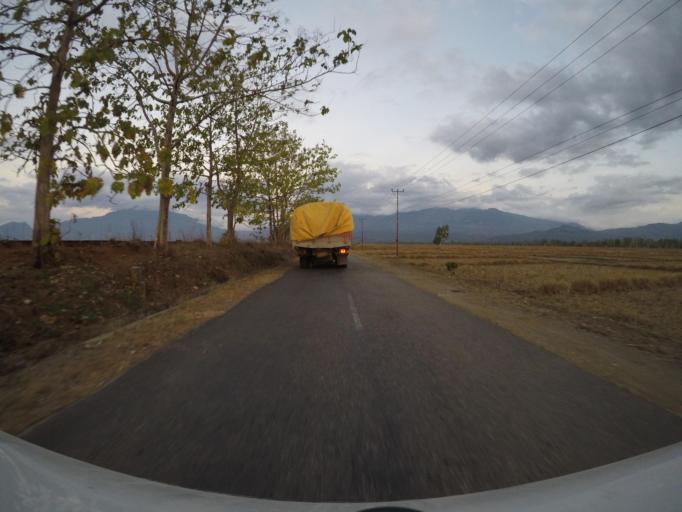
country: TL
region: Bobonaro
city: Maliana
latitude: -8.9806
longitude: 125.1513
